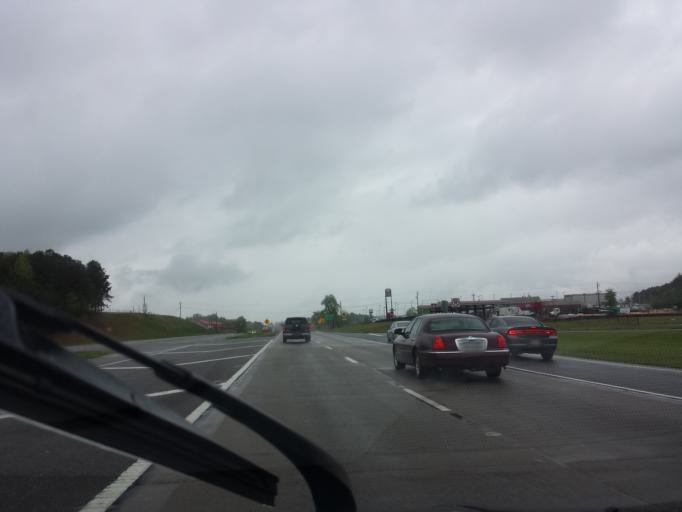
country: US
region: Georgia
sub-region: Pickens County
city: Jasper
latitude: 34.4548
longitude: -84.4529
